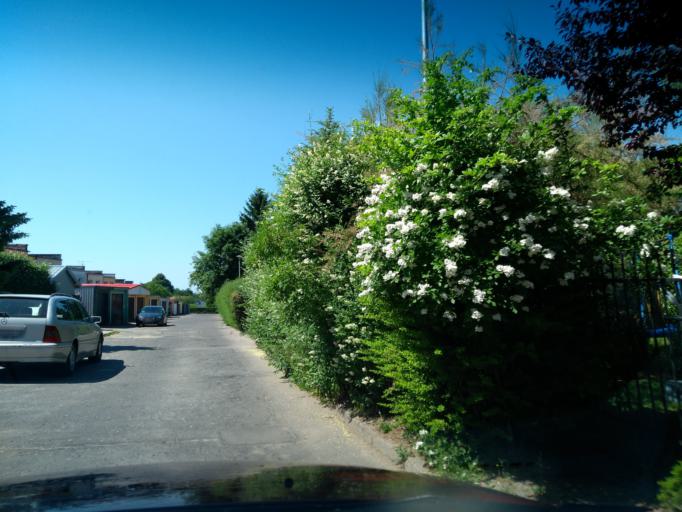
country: PL
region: West Pomeranian Voivodeship
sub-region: Koszalin
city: Koszalin
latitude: 54.2087
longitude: 16.1810
